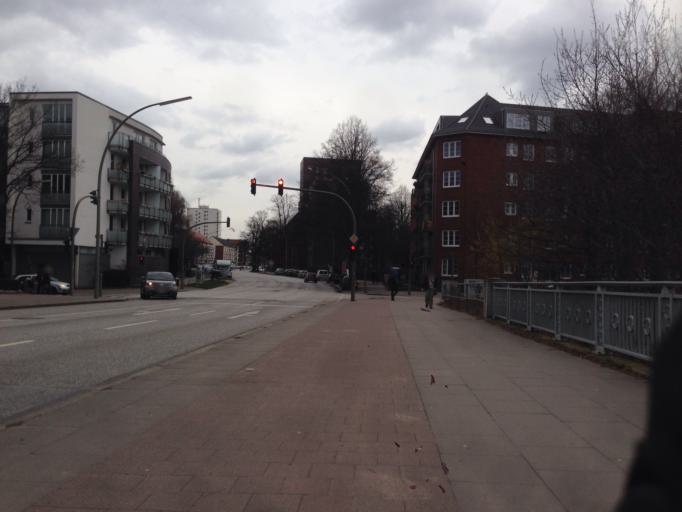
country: DE
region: Hamburg
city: Barmbek-Nord
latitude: 53.5850
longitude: 10.0421
